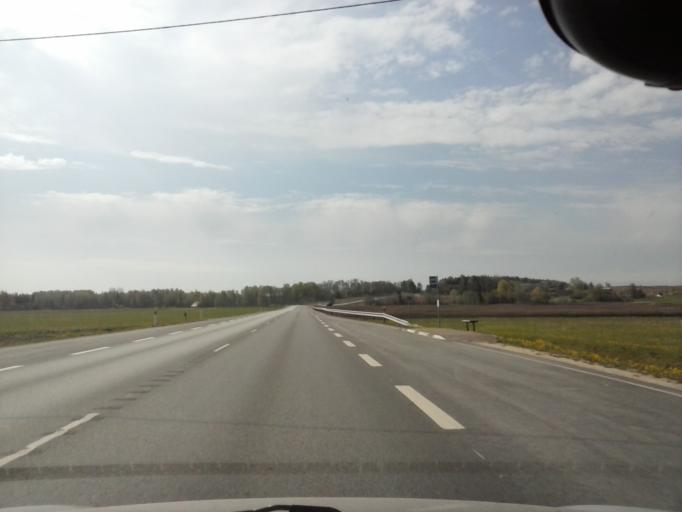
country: EE
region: Tartu
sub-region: UElenurme vald
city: Ulenurme
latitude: 58.2118
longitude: 26.7059
